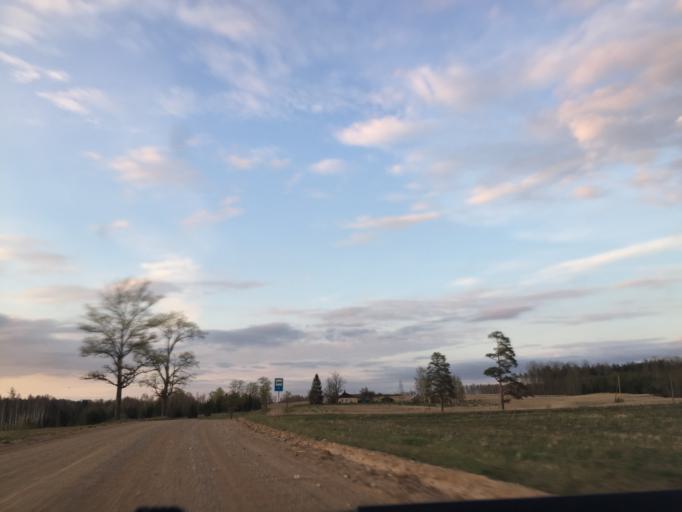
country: LV
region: Gulbenes Rajons
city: Gulbene
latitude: 57.2594
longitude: 26.9210
